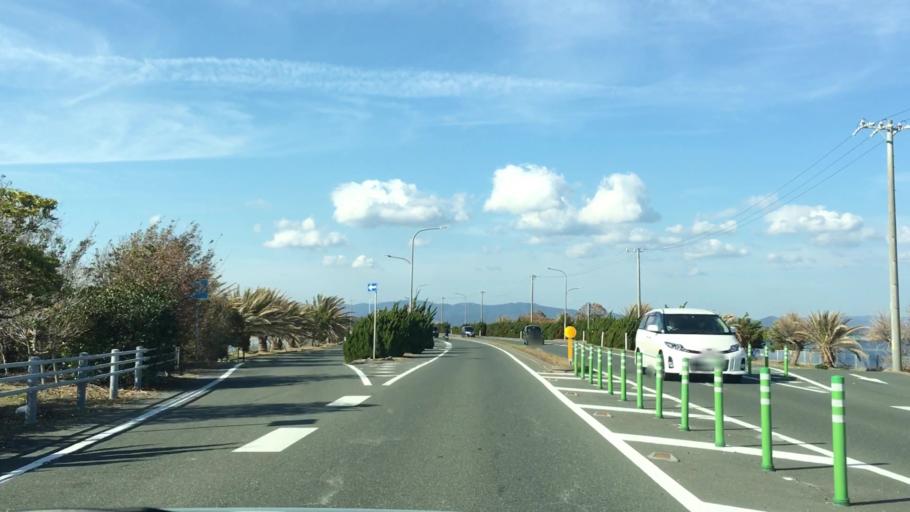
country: JP
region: Shizuoka
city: Kosai-shi
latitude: 34.7051
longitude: 137.6102
